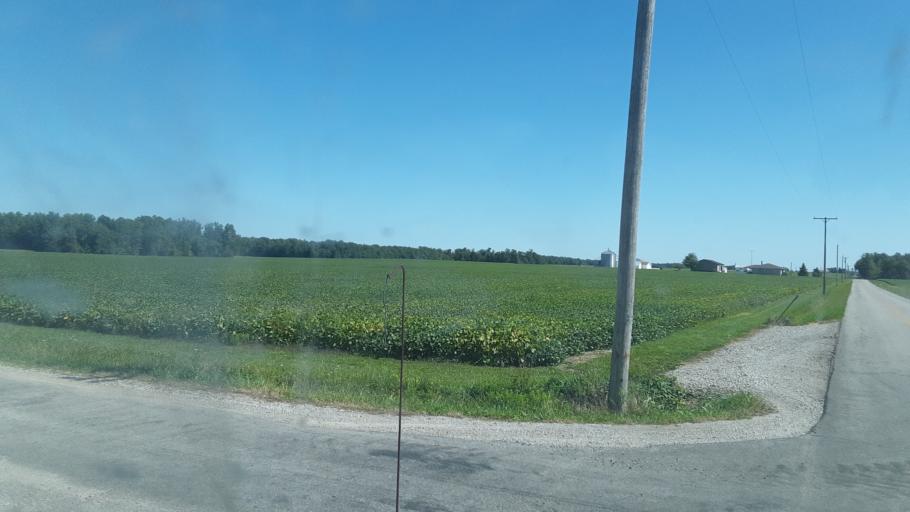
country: US
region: Ohio
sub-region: Sandusky County
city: Mount Carmel
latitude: 41.1610
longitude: -82.9000
